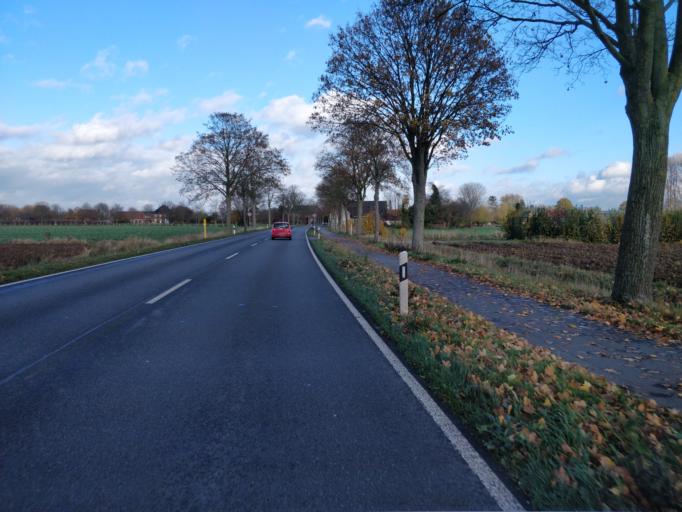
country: DE
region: North Rhine-Westphalia
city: Rees
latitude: 51.7735
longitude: 6.4170
